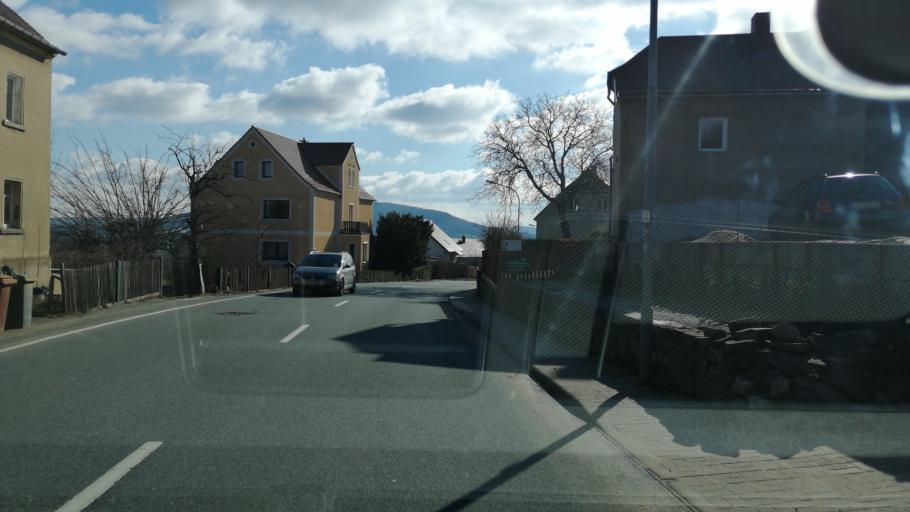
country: DE
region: Saxony
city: Lobau
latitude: 51.1269
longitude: 14.6764
